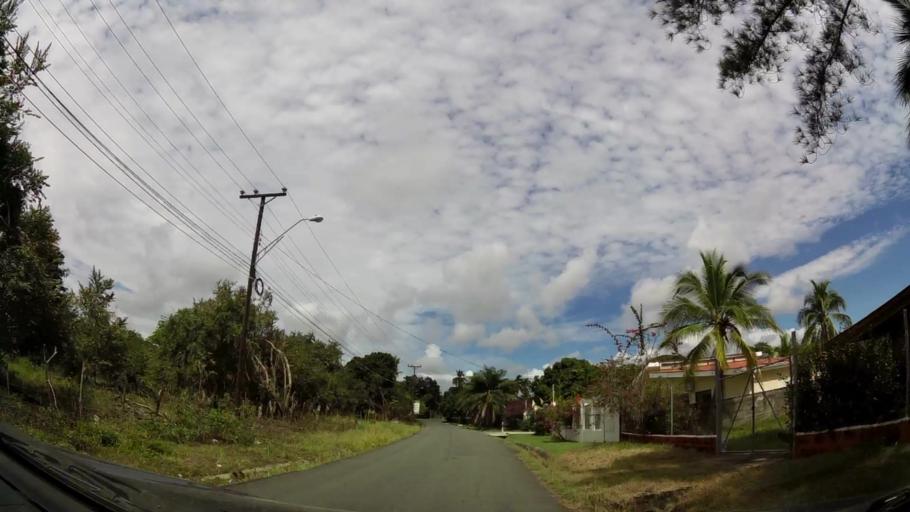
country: PA
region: Panama
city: Nueva Gorgona
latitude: 8.5329
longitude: -79.9182
